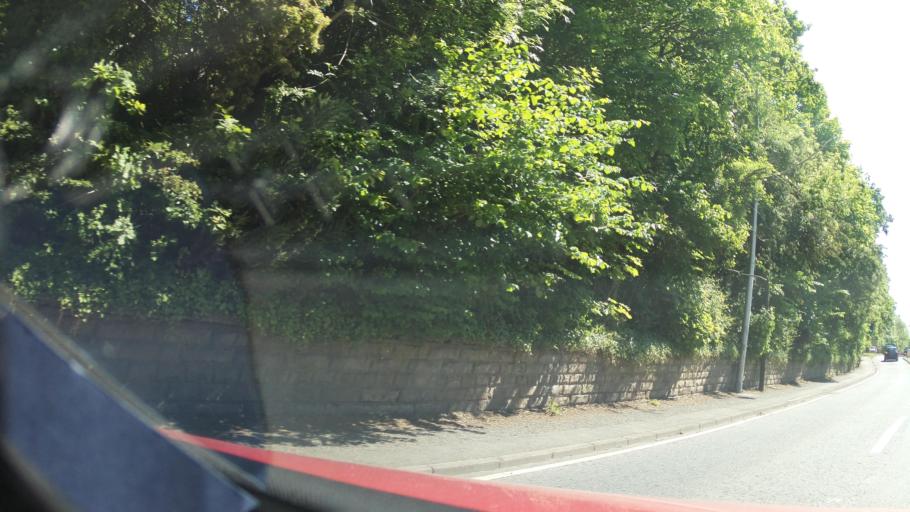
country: GB
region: Scotland
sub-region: Midlothian
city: Dalkeith
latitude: 55.8720
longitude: -3.0761
